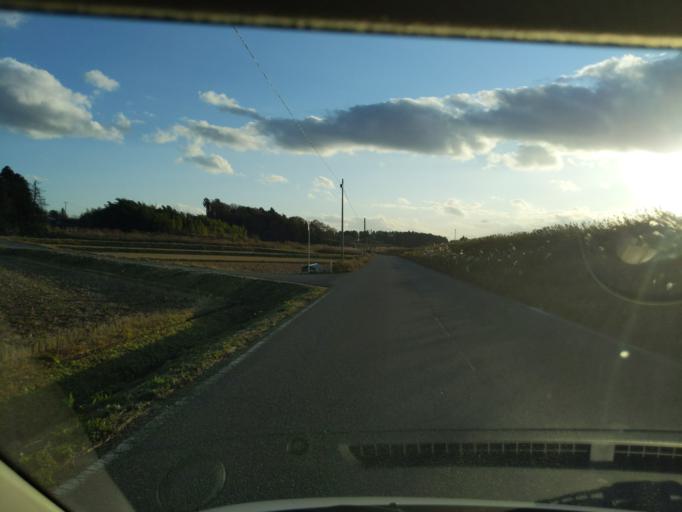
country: JP
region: Miyagi
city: Kogota
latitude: 38.6297
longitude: 141.0686
